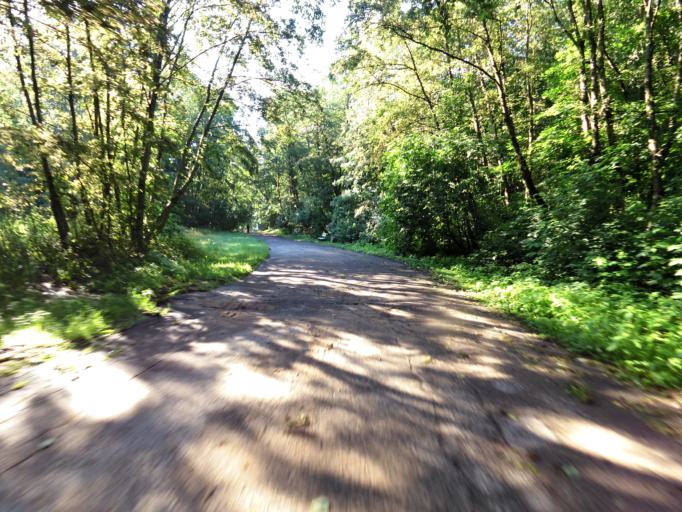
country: LT
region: Vilnius County
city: Seskine
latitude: 54.7064
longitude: 25.2472
